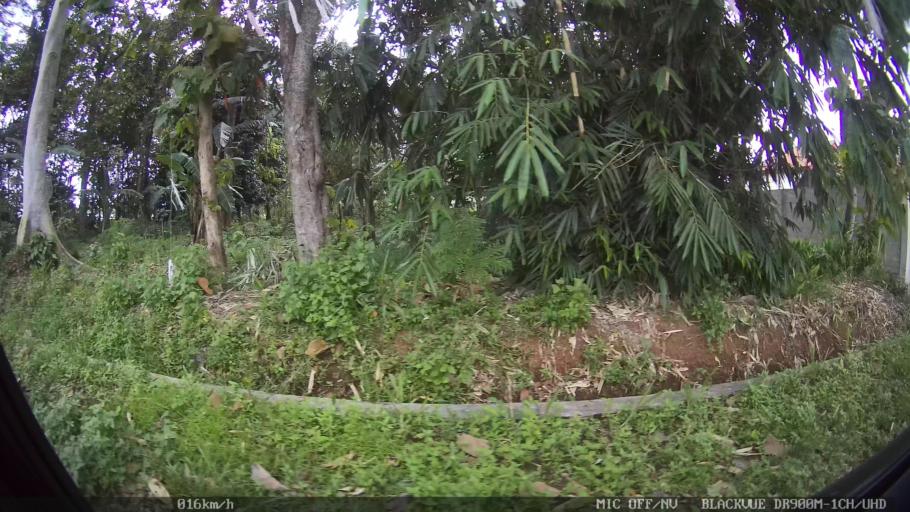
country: ID
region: Lampung
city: Gadingrejo
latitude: -5.3656
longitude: 105.0647
